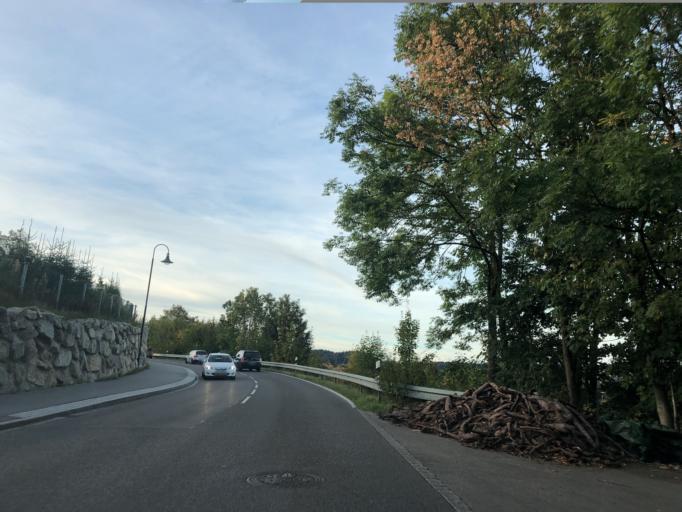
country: DE
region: Bavaria
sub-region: Swabia
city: Pfronten
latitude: 47.5876
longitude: 10.5598
